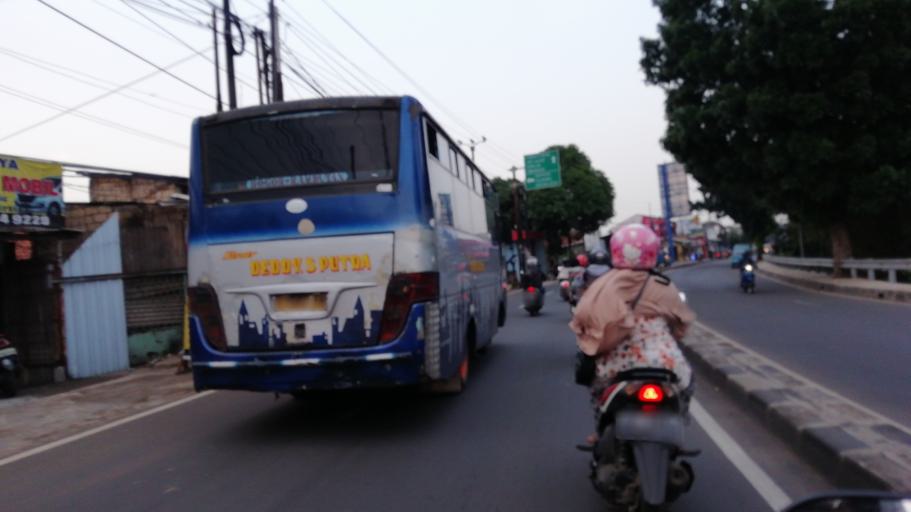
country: ID
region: West Java
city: Cibinong
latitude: -6.4372
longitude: 106.8522
